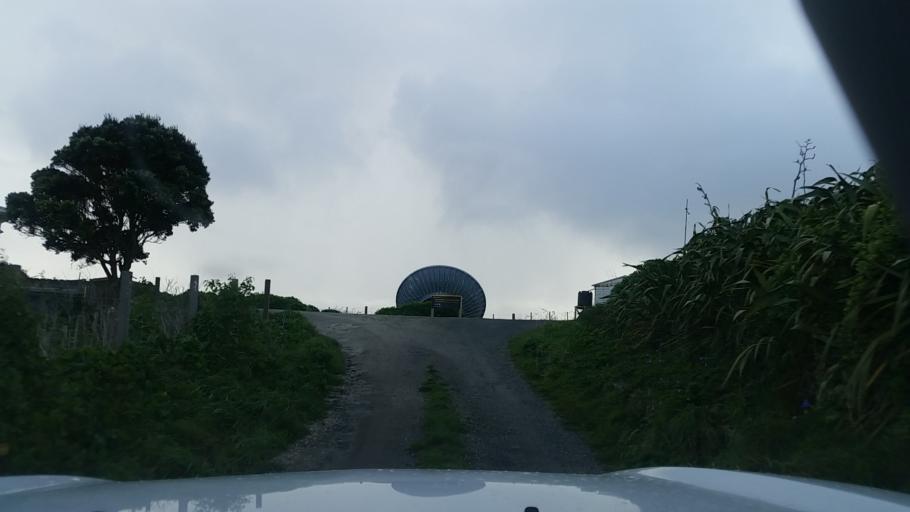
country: NZ
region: Chatham Islands
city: Waitangi
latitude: -43.9463
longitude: -176.5629
